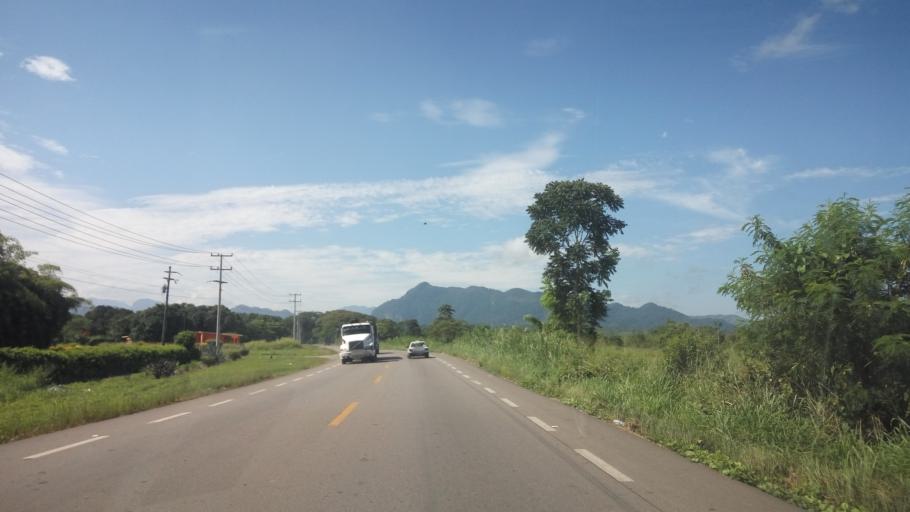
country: MX
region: Tabasco
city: Teapa
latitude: 17.5873
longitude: -92.9671
